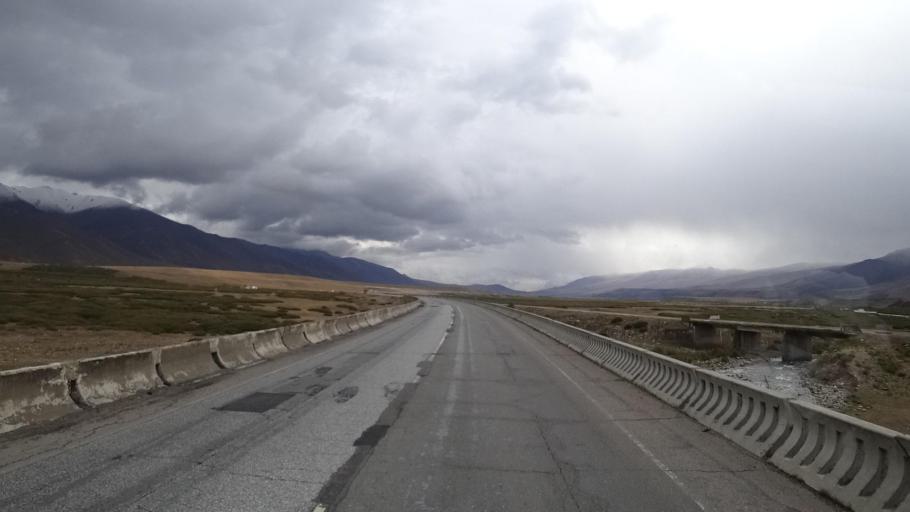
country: KG
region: Jalal-Abad
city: Uch-Terek
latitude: 42.1876
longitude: 73.4103
